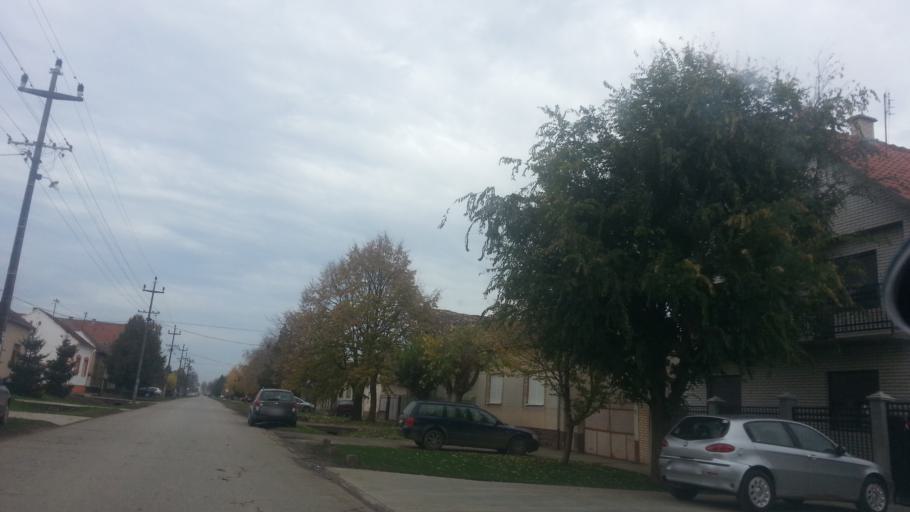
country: RS
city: Golubinci
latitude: 44.9906
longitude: 20.0619
